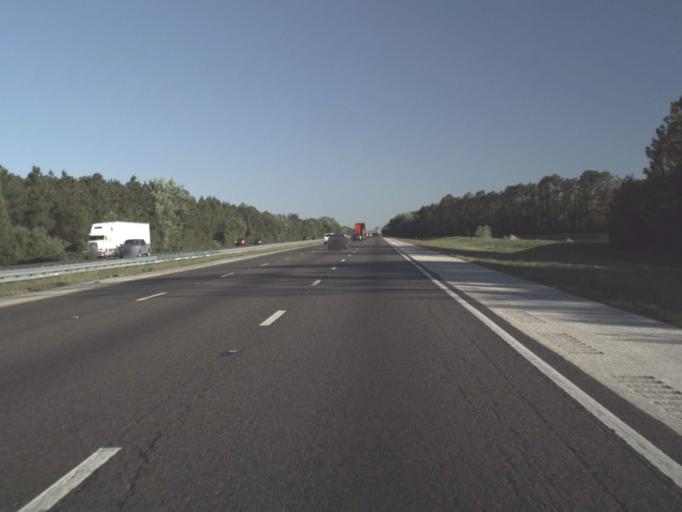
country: US
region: Florida
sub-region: Flagler County
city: Palm Coast
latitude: 29.6237
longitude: -81.2613
